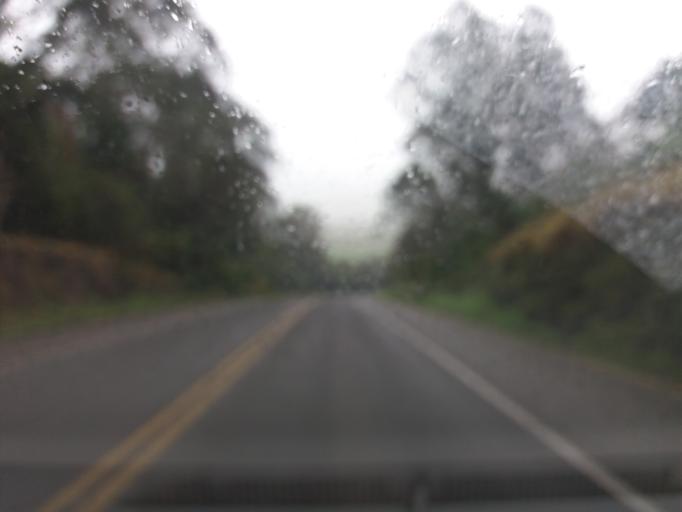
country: BR
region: Parana
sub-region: Francisco Beltrao
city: Francisco Beltrao
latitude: -26.0885
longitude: -53.2641
